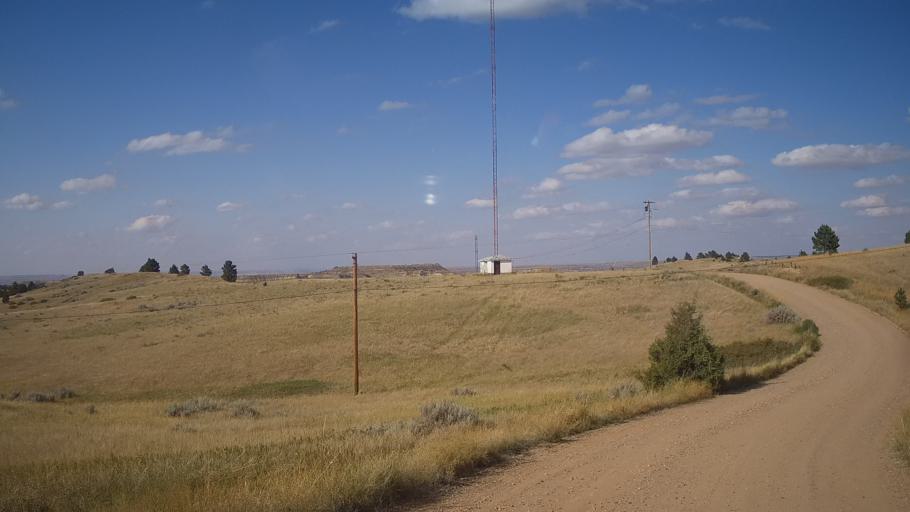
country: US
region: Montana
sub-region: Dawson County
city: Glendive
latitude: 47.0515
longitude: -104.6755
